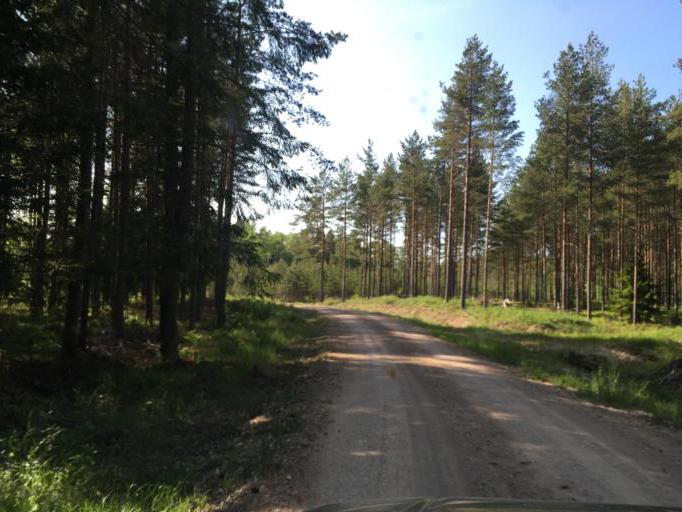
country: LV
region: Dundaga
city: Dundaga
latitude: 57.6111
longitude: 22.5132
